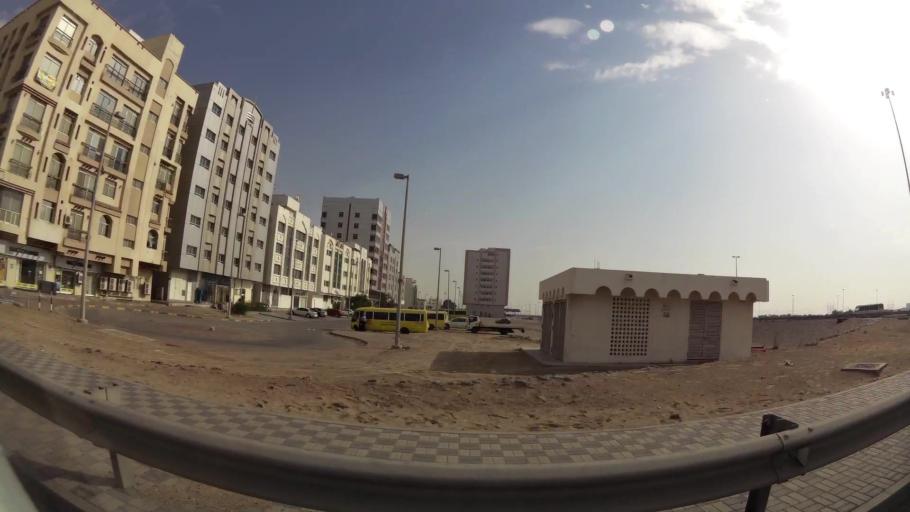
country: AE
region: Abu Dhabi
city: Abu Dhabi
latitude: 24.3246
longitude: 54.5306
